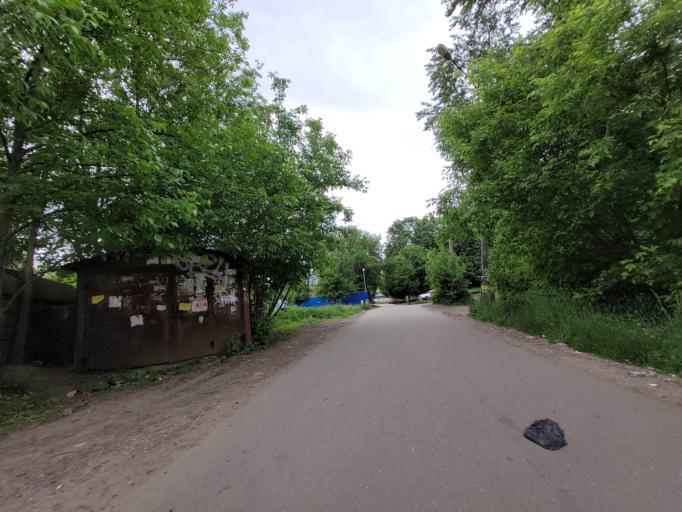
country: RU
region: Moskovskaya
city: Lesnyye Polyany
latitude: 55.9455
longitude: 37.8624
